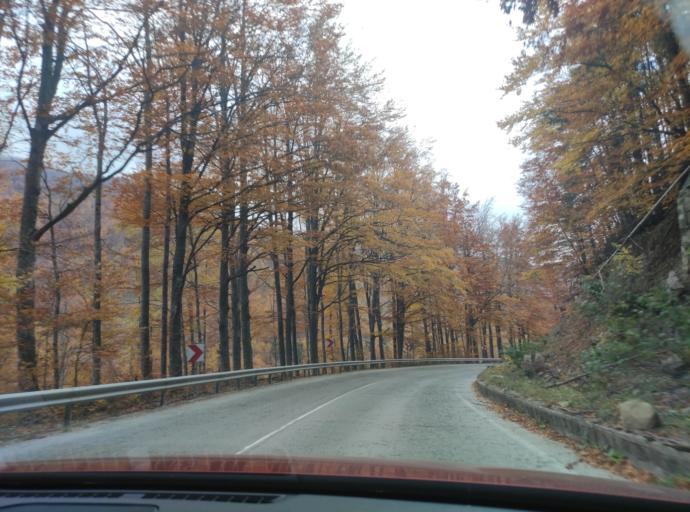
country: BG
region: Montana
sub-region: Obshtina Berkovitsa
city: Berkovitsa
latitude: 43.1375
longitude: 23.1422
